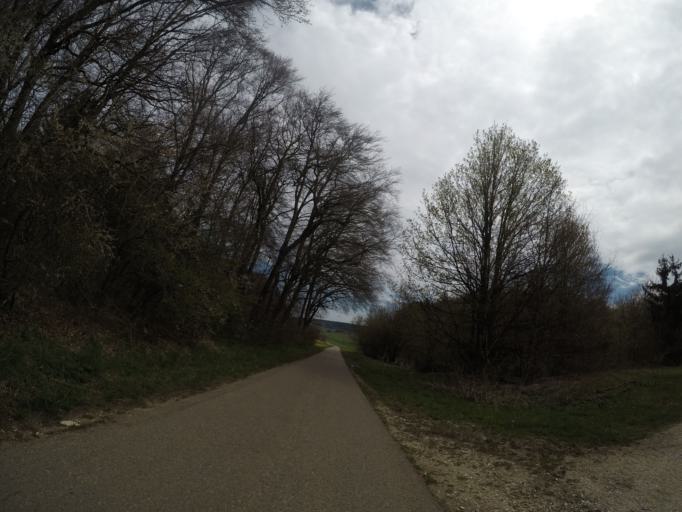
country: DE
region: Baden-Wuerttemberg
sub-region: Tuebingen Region
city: Westerheim
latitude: 48.5107
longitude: 9.6335
